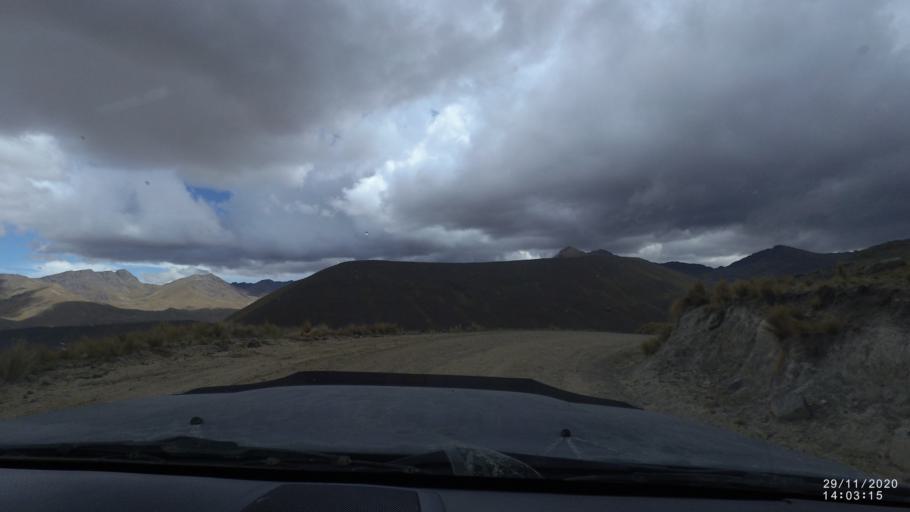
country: BO
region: Cochabamba
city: Sipe Sipe
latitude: -17.1946
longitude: -66.3751
